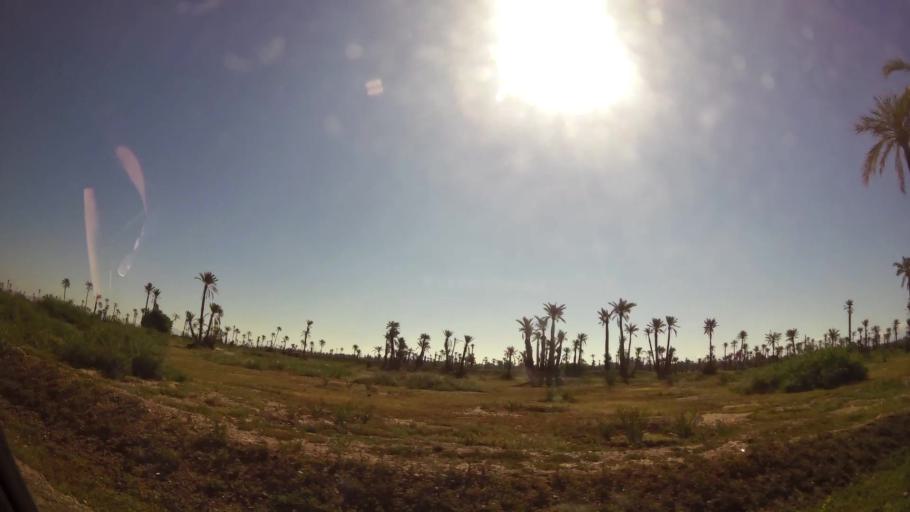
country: MA
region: Marrakech-Tensift-Al Haouz
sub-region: Marrakech
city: Marrakesh
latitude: 31.6614
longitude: -7.9535
